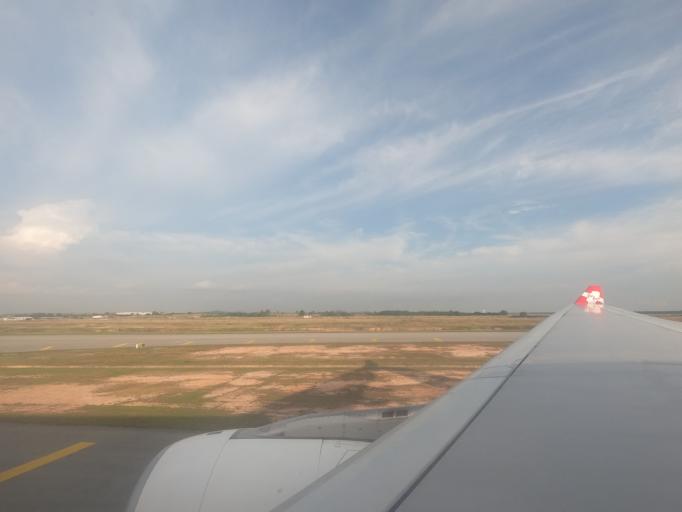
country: MY
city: Sungai Pelek New Village
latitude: 2.7366
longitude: 101.6876
